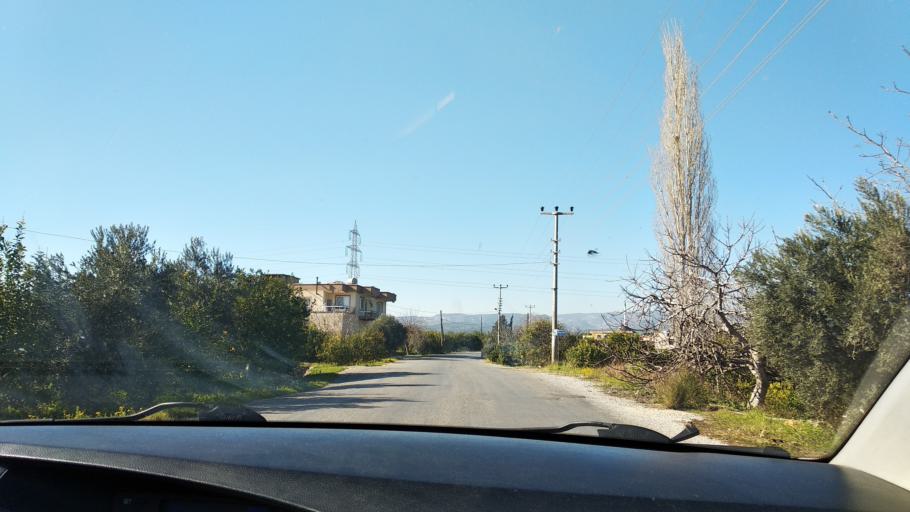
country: TR
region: Mersin
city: Tomuk
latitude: 36.6632
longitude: 34.3630
